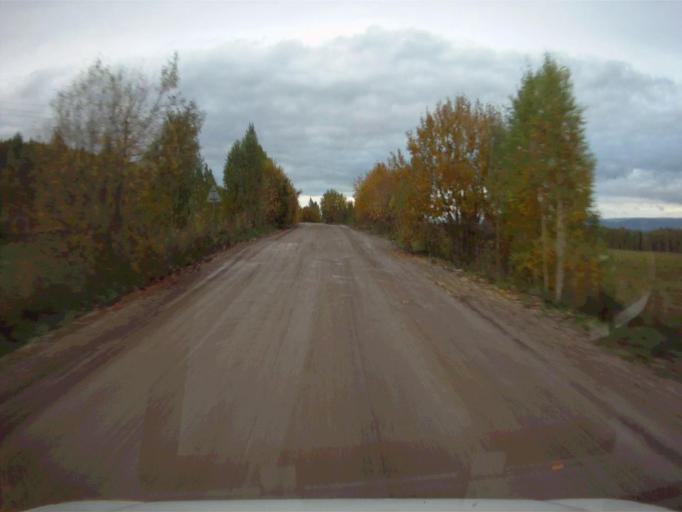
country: RU
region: Sverdlovsk
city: Mikhaylovsk
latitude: 56.2005
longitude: 59.2003
